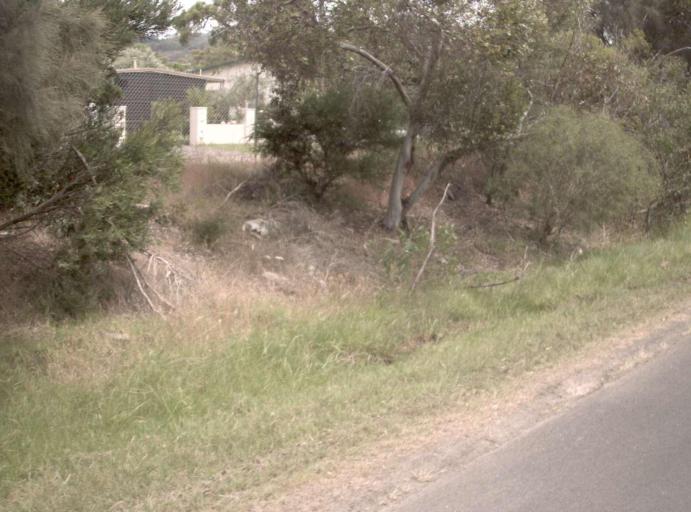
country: AU
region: Victoria
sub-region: Mornington Peninsula
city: Dromana
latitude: -38.3354
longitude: 144.9771
